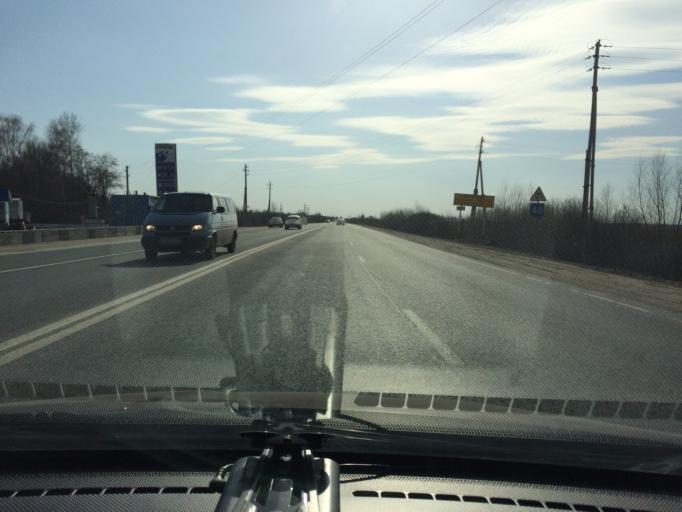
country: RU
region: Mariy-El
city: Yoshkar-Ola
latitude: 56.6773
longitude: 48.0177
